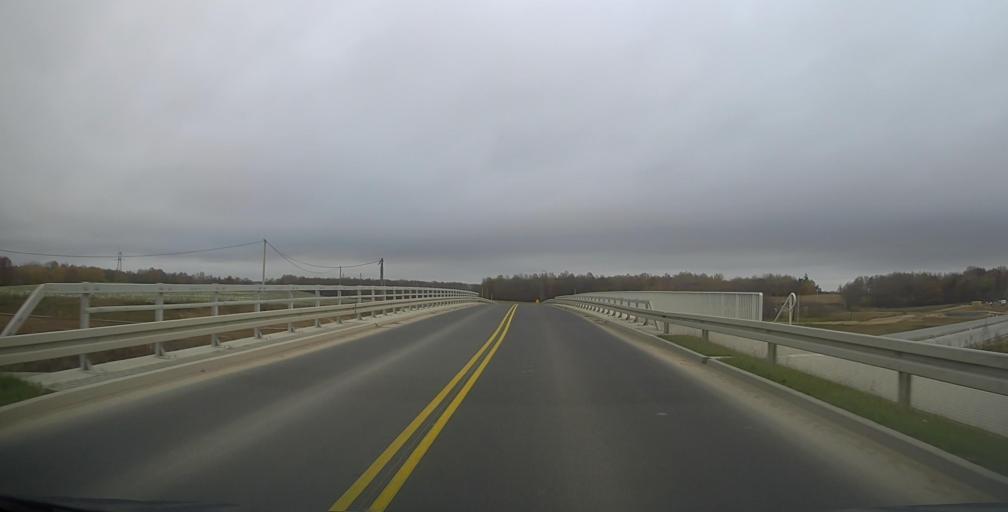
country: PL
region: Warmian-Masurian Voivodeship
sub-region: Powiat elcki
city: Elk
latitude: 53.8546
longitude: 22.4953
